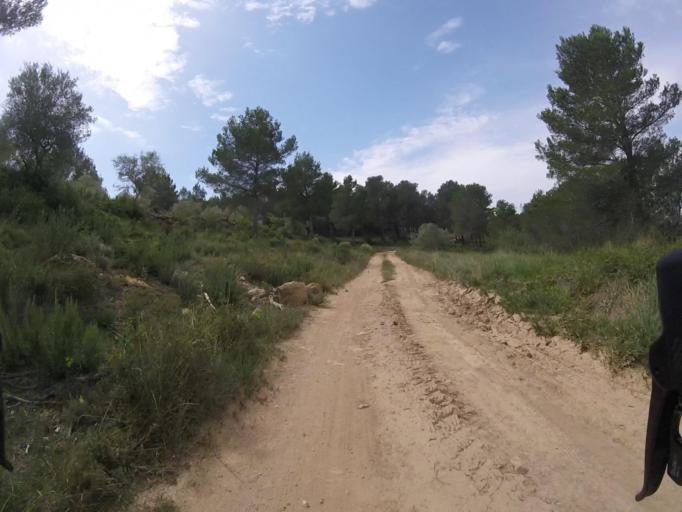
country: ES
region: Valencia
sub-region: Provincia de Castello
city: Cuevas de Vinroma
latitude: 40.2711
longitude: 0.1162
